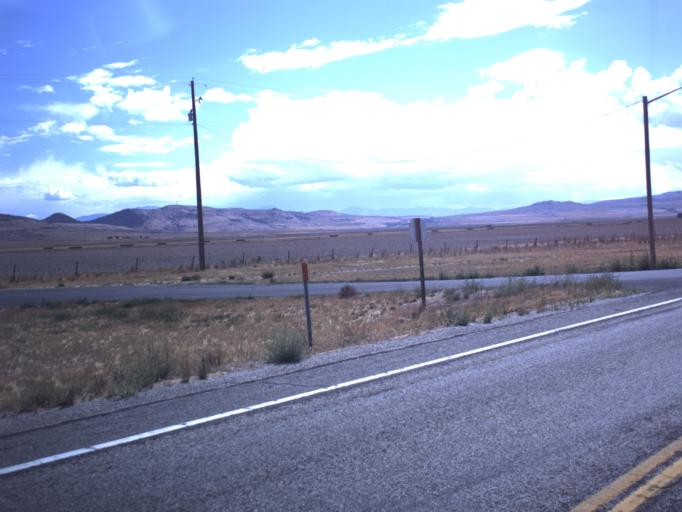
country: US
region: Utah
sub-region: Box Elder County
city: Garland
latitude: 41.8703
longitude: -112.1475
